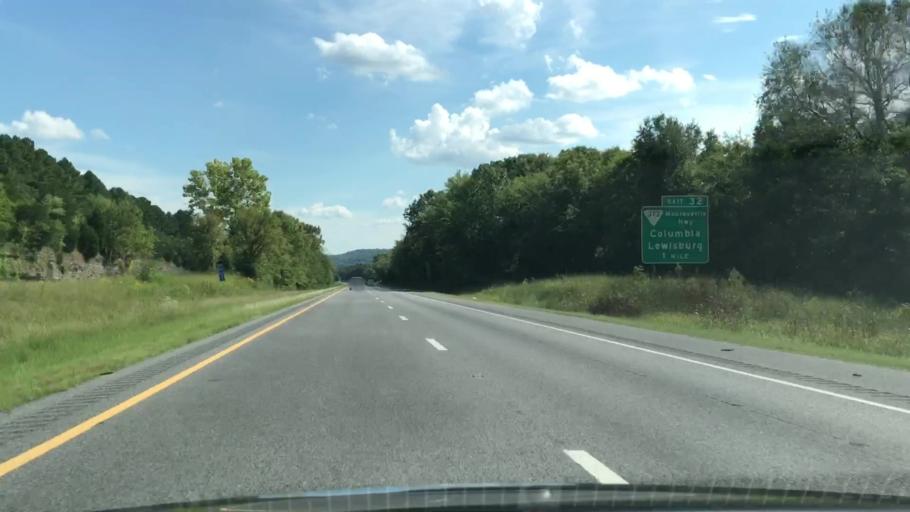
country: US
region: Tennessee
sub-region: Marshall County
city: Lewisburg
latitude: 35.4661
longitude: -86.8872
